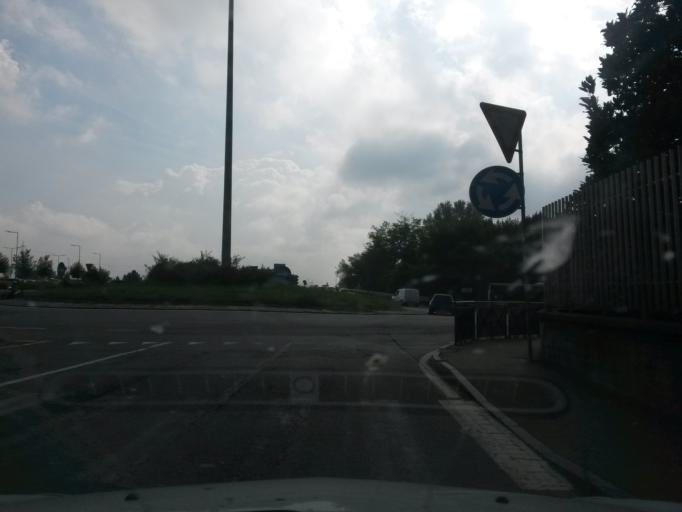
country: IT
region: Piedmont
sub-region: Provincia di Torino
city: Tetti Neirotti
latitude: 45.0652
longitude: 7.5406
